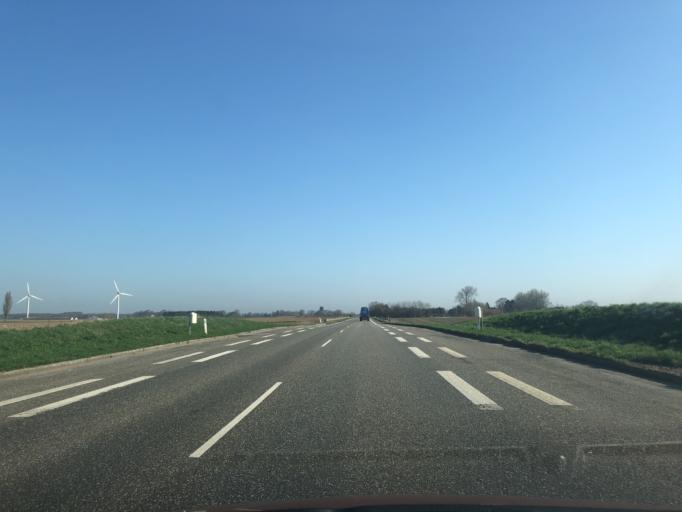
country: DK
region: Zealand
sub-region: Faxe Kommune
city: Ronnede
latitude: 55.2750
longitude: 12.0303
